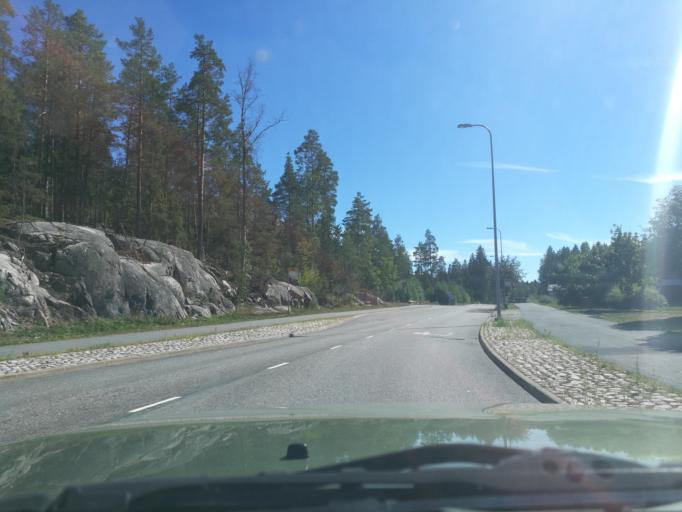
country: FI
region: Uusimaa
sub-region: Helsinki
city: Kerava
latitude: 60.3564
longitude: 25.1367
